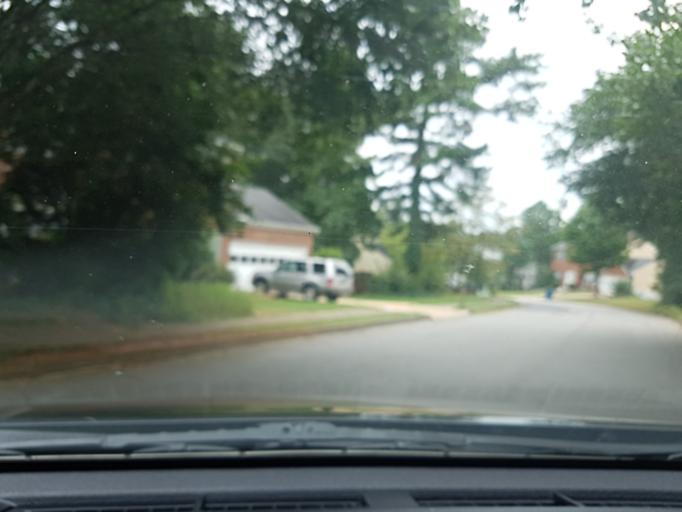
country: US
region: Georgia
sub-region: Gwinnett County
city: Duluth
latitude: 33.9838
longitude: -84.1525
